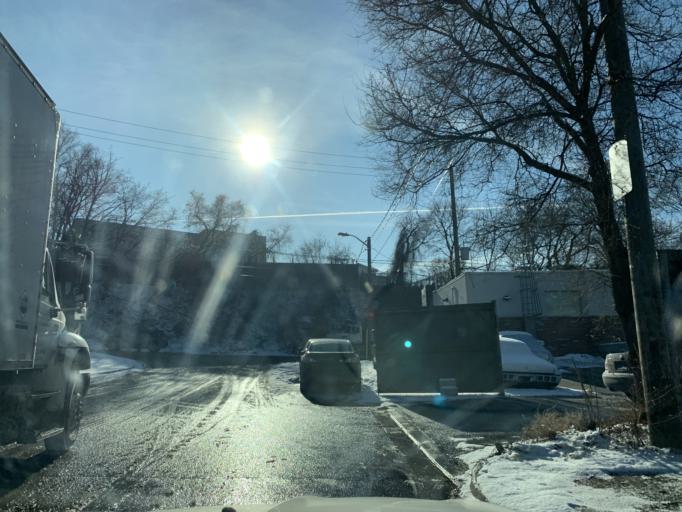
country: CA
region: Ontario
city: Toronto
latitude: 43.6836
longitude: -79.4763
